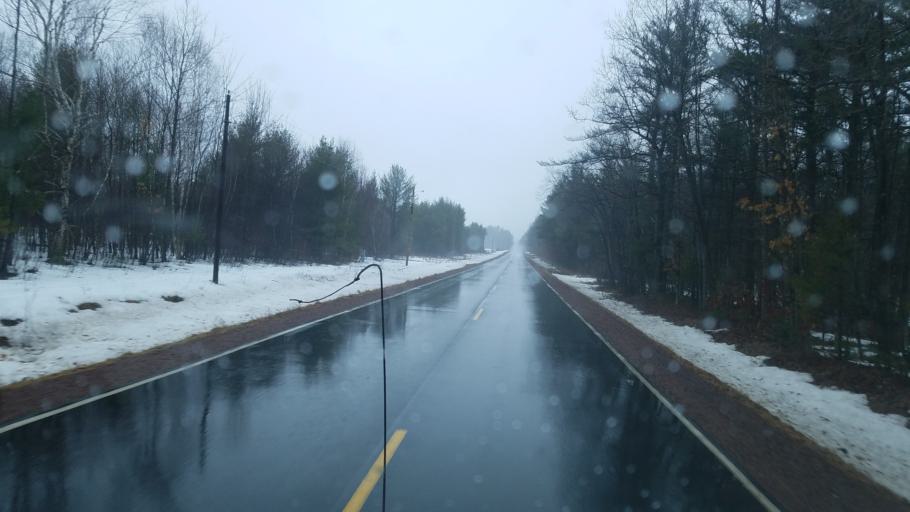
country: US
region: Wisconsin
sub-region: Wood County
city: Marshfield
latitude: 44.5168
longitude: -90.2994
